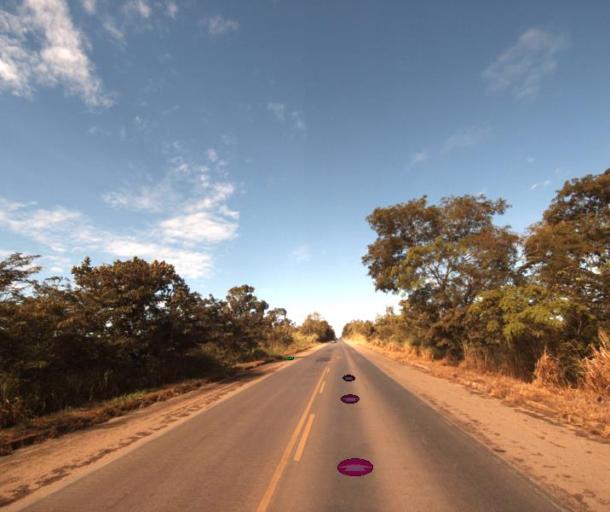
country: BR
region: Goias
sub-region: Itapaci
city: Itapaci
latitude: -14.8181
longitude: -49.2961
